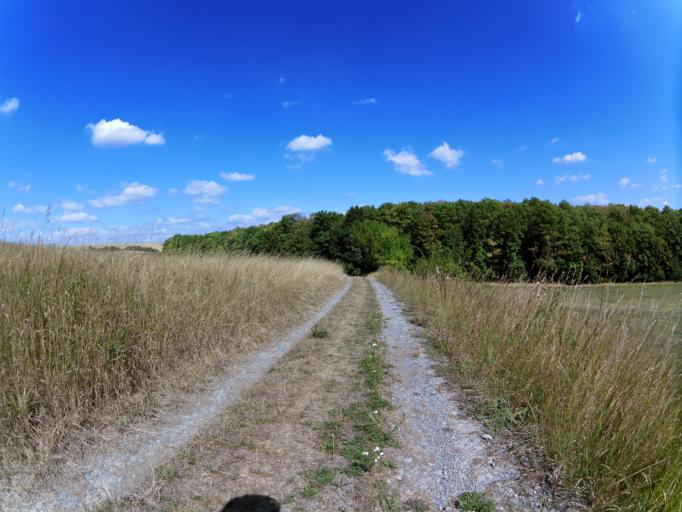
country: DE
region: Bavaria
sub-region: Regierungsbezirk Unterfranken
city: Zell am Main
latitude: 49.8015
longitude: 9.8601
